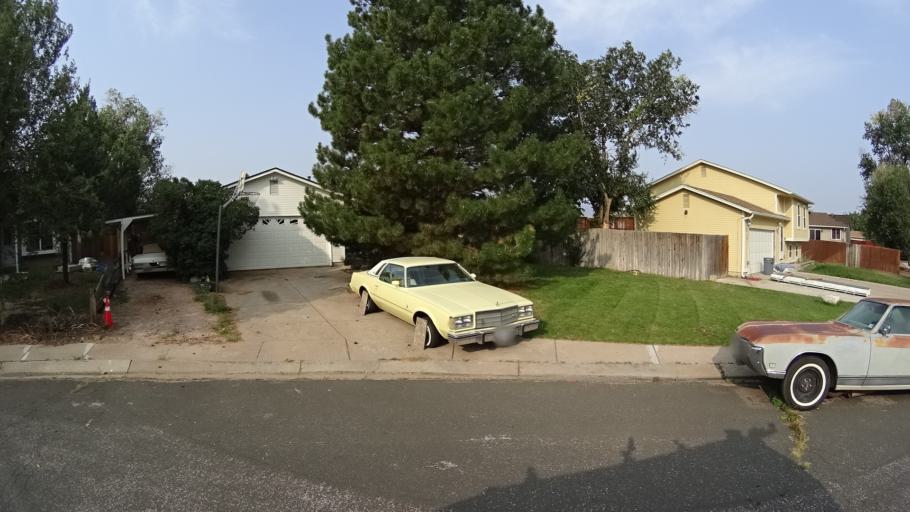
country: US
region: Colorado
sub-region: El Paso County
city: Stratmoor
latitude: 38.8032
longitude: -104.7433
